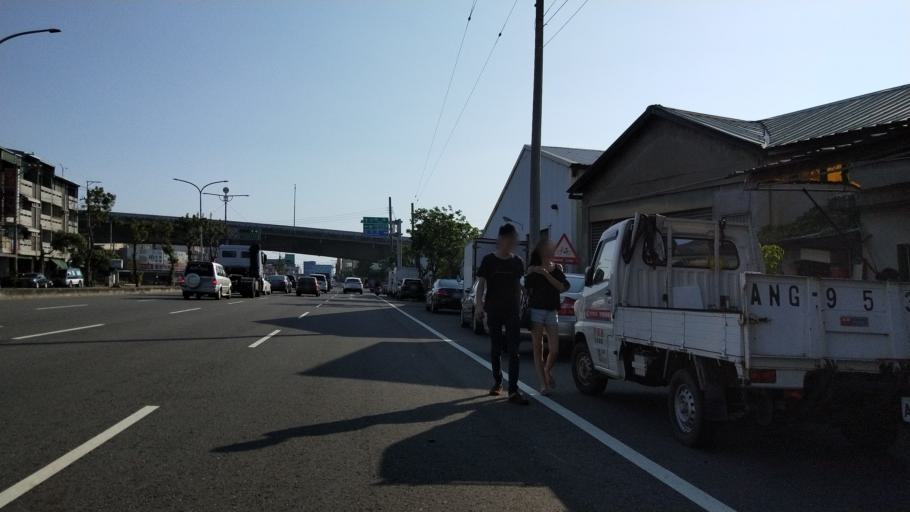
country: TW
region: Taiwan
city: Fengyuan
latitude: 24.2715
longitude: 120.5679
